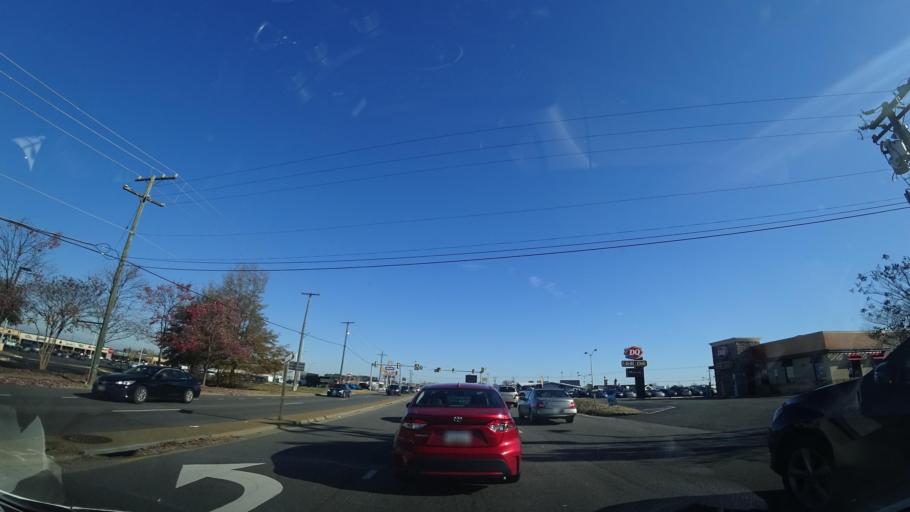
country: US
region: Virginia
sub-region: City of Fredericksburg
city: Fredericksburg
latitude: 38.2539
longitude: -77.5001
